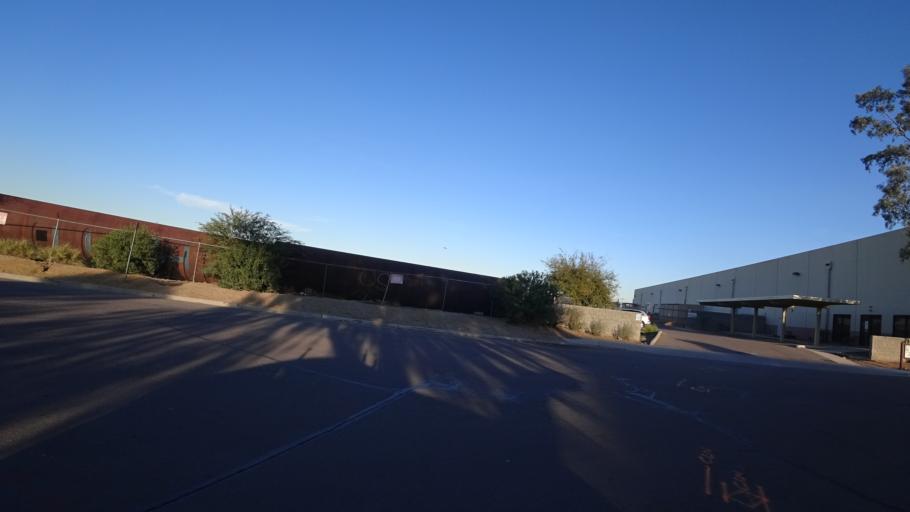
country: US
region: Arizona
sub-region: Maricopa County
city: Phoenix
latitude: 33.4251
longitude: -112.0602
